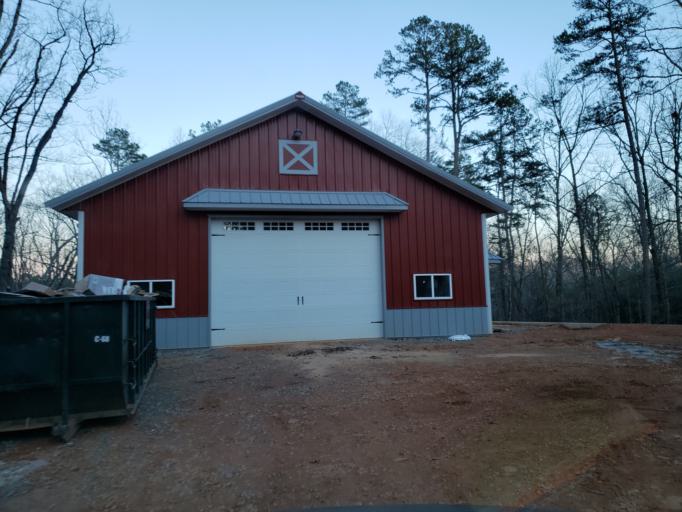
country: US
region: Georgia
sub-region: Pickens County
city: Nelson
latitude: 34.3756
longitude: -84.3603
